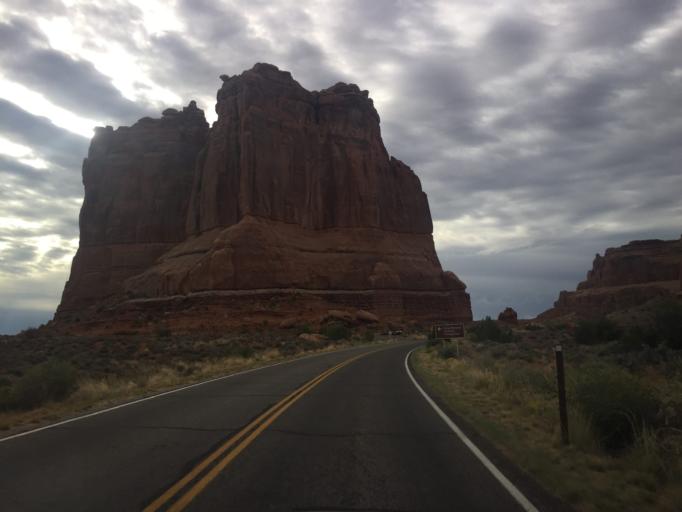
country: US
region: Utah
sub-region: Grand County
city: Moab
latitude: 38.6383
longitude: -109.6015
